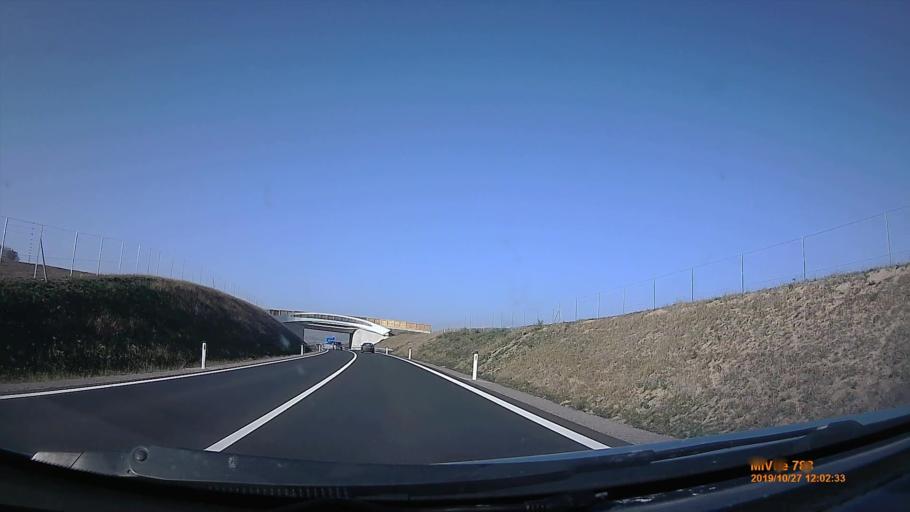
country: AT
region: Lower Austria
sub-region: Politischer Bezirk Mistelbach
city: Drasenhofen
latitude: 48.7357
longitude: 16.6502
